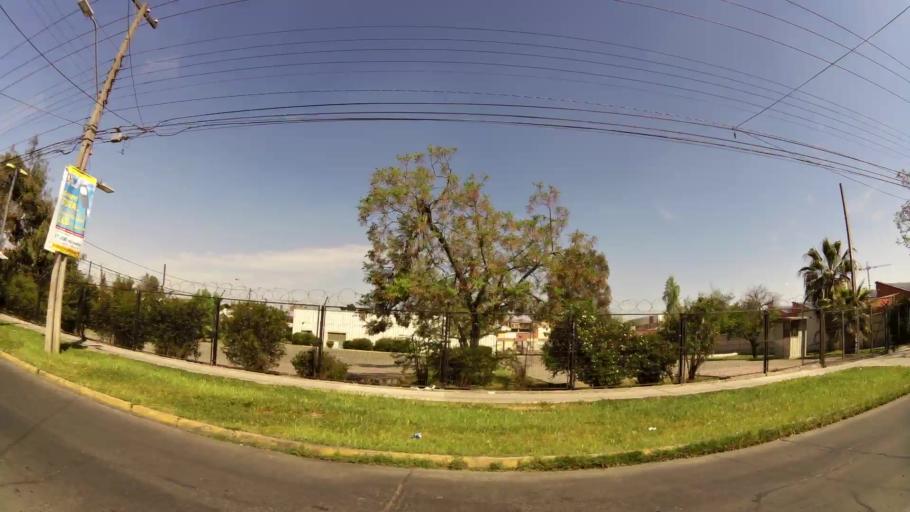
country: CL
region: Santiago Metropolitan
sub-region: Provincia de Santiago
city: La Pintana
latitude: -33.5223
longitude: -70.6511
